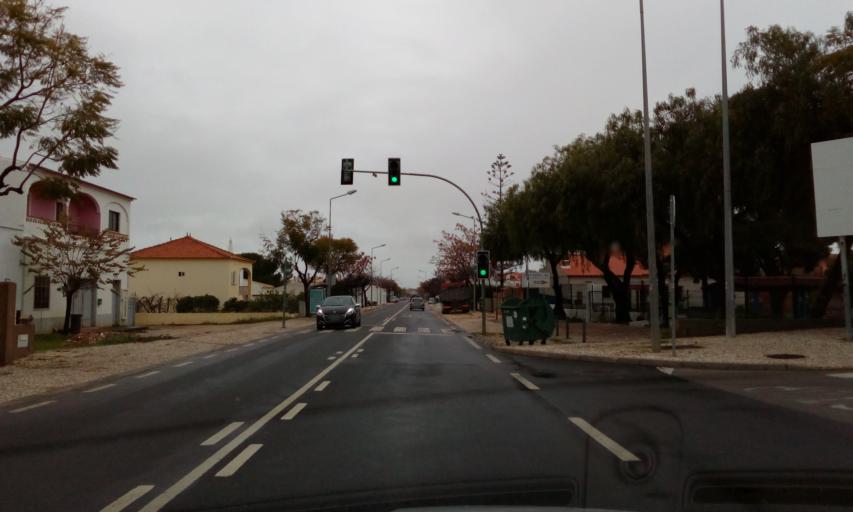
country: PT
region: Faro
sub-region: Albufeira
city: Ferreiras
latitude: 37.1253
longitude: -8.2323
